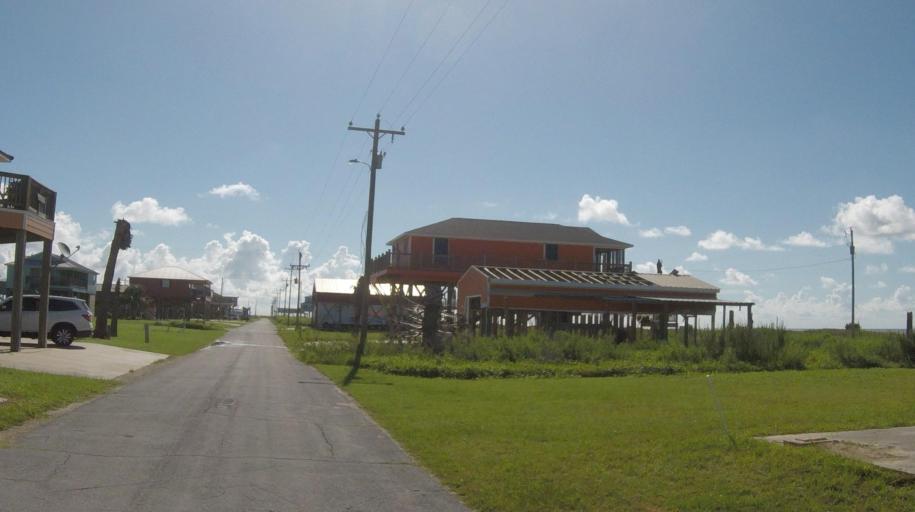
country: US
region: Louisiana
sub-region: Cameron Parish
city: Cameron
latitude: 29.7704
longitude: -93.4525
